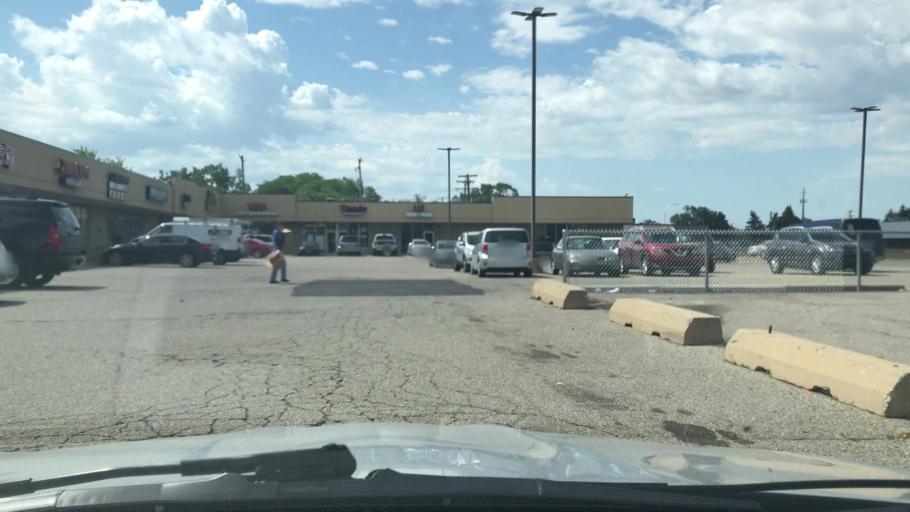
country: US
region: Michigan
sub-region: Oakland County
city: Clawson
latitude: 42.5270
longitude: -83.1059
